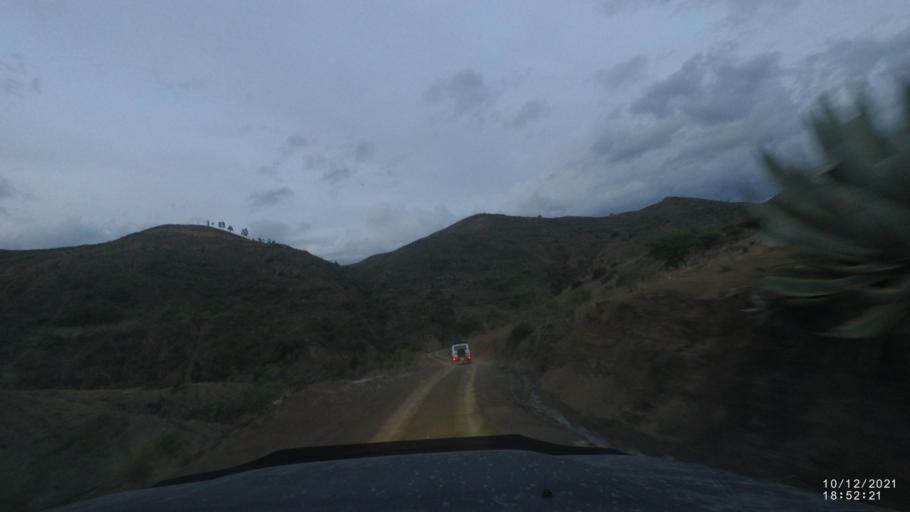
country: BO
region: Cochabamba
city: Tarata
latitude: -17.8831
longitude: -65.9634
